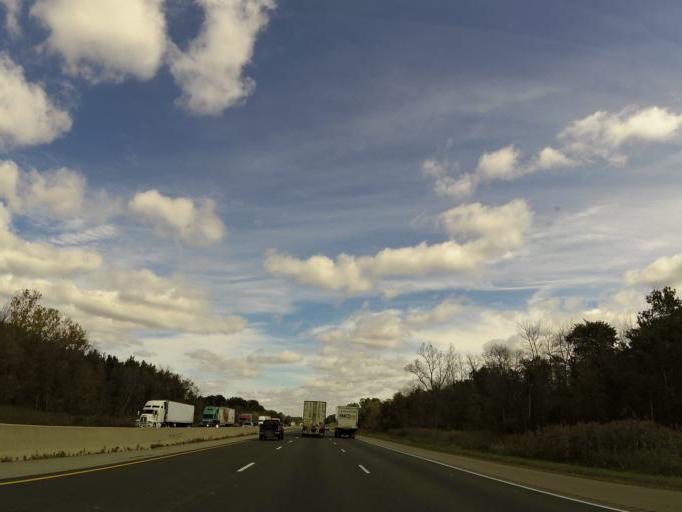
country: CA
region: Ontario
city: Dorchester
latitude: 42.9680
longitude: -81.0006
